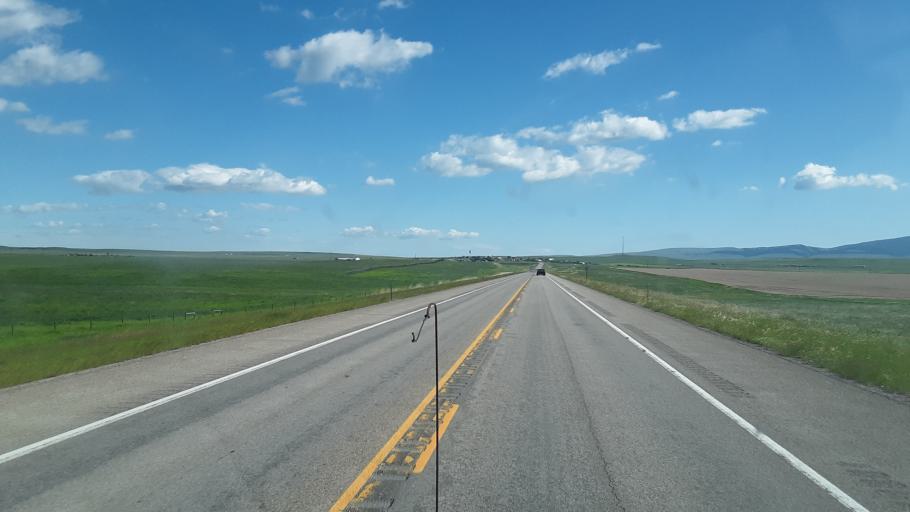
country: US
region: Montana
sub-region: Wheatland County
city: Harlowton
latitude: 46.6543
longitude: -109.7590
